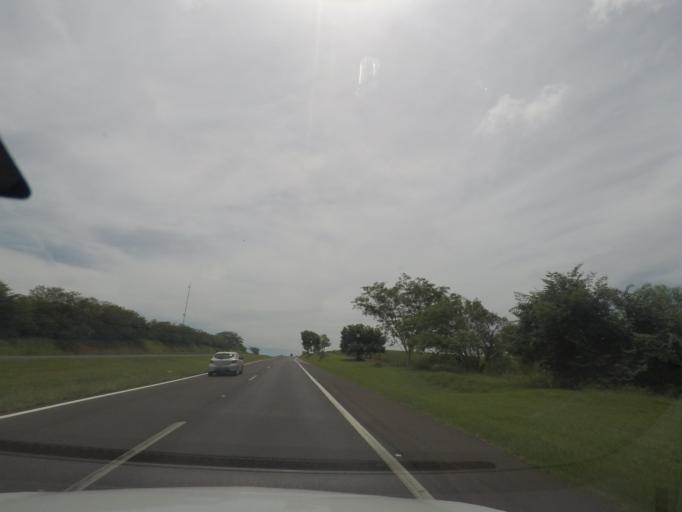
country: BR
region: Sao Paulo
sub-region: Bebedouro
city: Bebedouro
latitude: -20.9705
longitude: -48.4401
